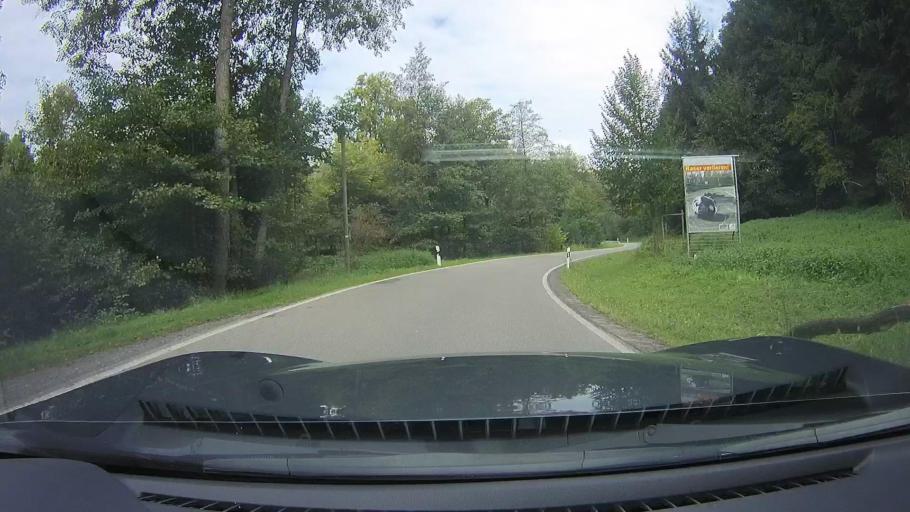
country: DE
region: Baden-Wuerttemberg
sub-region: Regierungsbezirk Stuttgart
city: Spiegelberg
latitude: 49.0461
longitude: 9.4479
